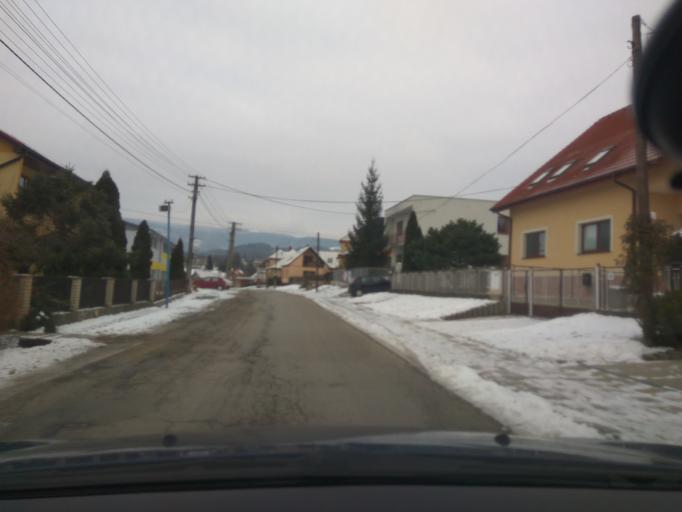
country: SK
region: Nitriansky
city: Stara Tura
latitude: 48.8046
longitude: 17.7129
